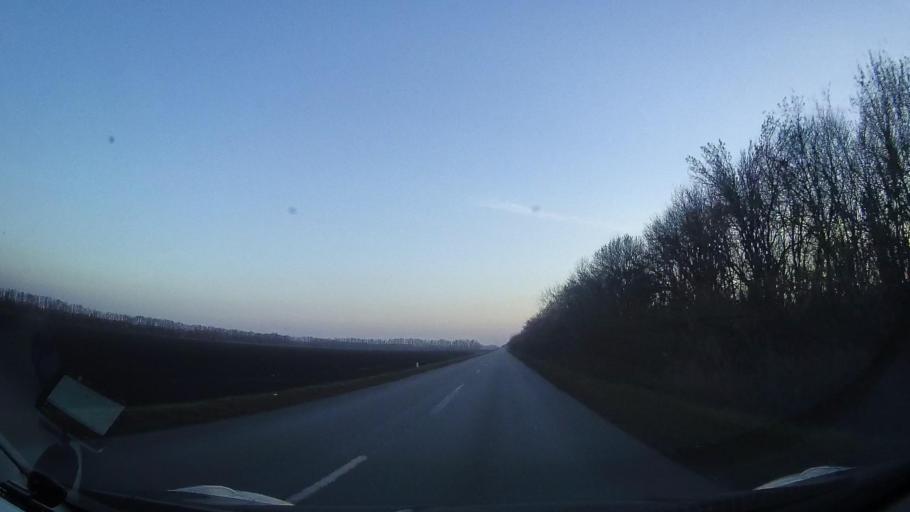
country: RU
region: Rostov
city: Zernograd
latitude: 47.0177
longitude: 40.3917
